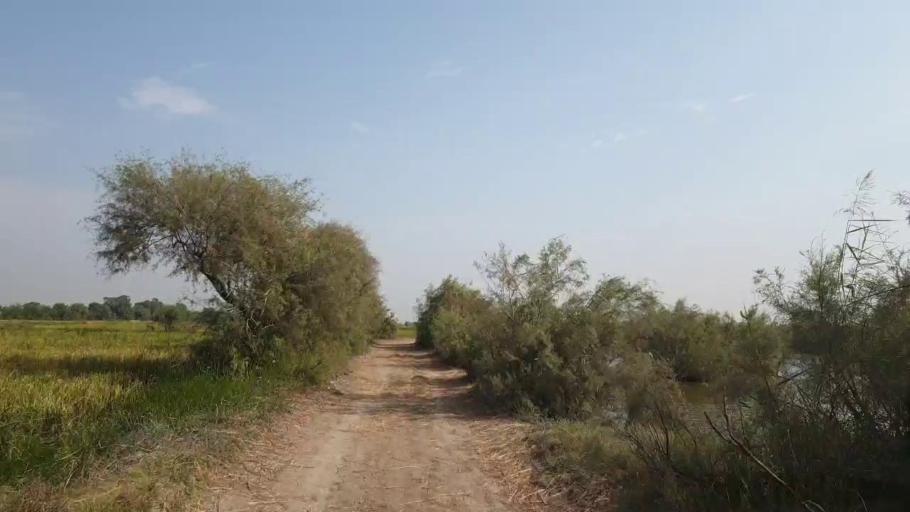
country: PK
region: Sindh
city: Tando Muhammad Khan
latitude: 25.0603
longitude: 68.4263
